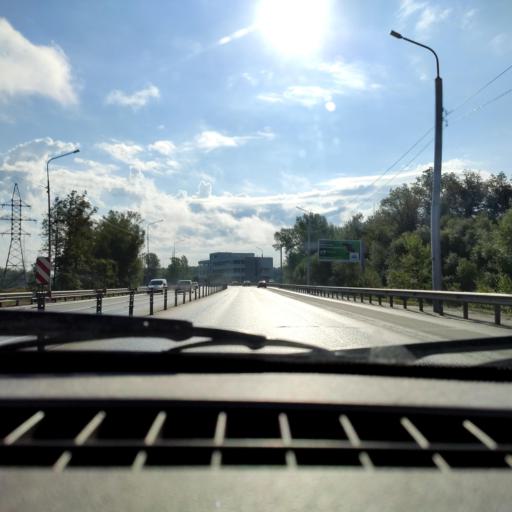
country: RU
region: Bashkortostan
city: Ufa
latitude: 54.6973
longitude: 55.8905
